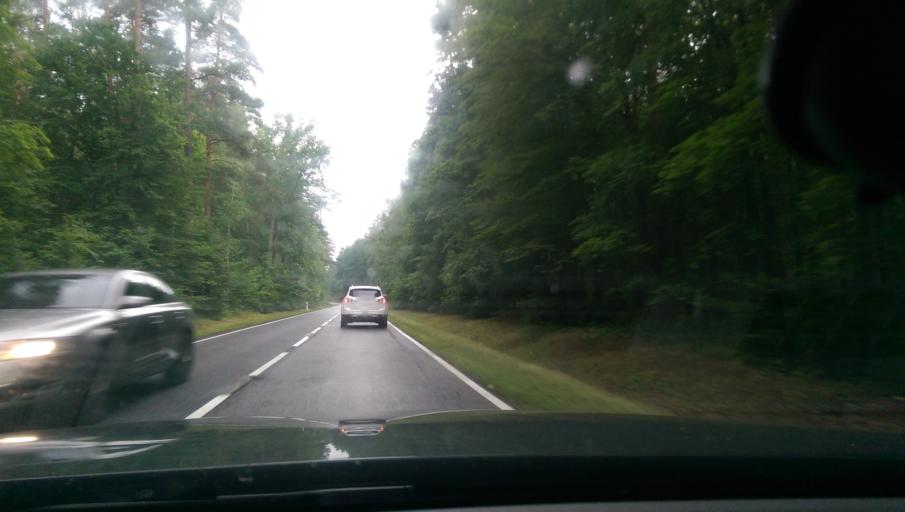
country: PL
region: Warmian-Masurian Voivodeship
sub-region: Powiat szczycienski
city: Szczytno
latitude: 53.5255
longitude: 20.9785
